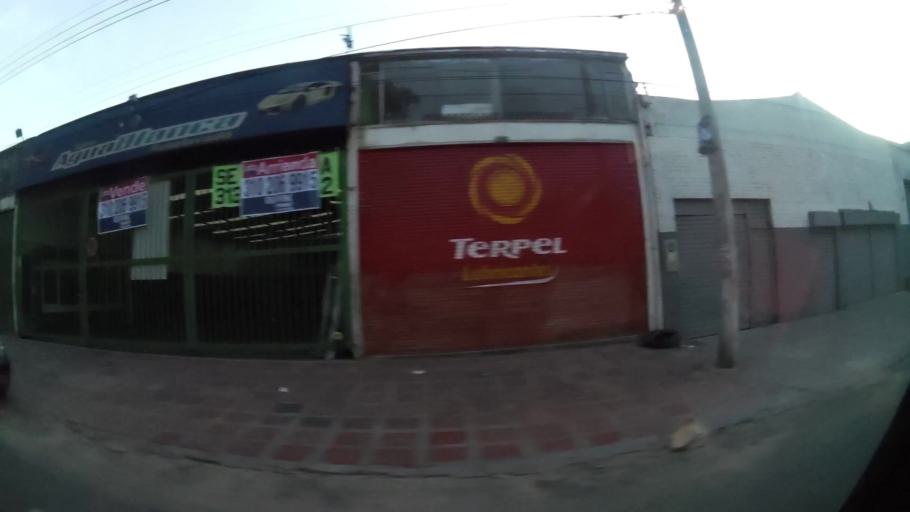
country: CO
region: Bogota D.C.
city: Barrio San Luis
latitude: 4.6554
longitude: -74.0641
